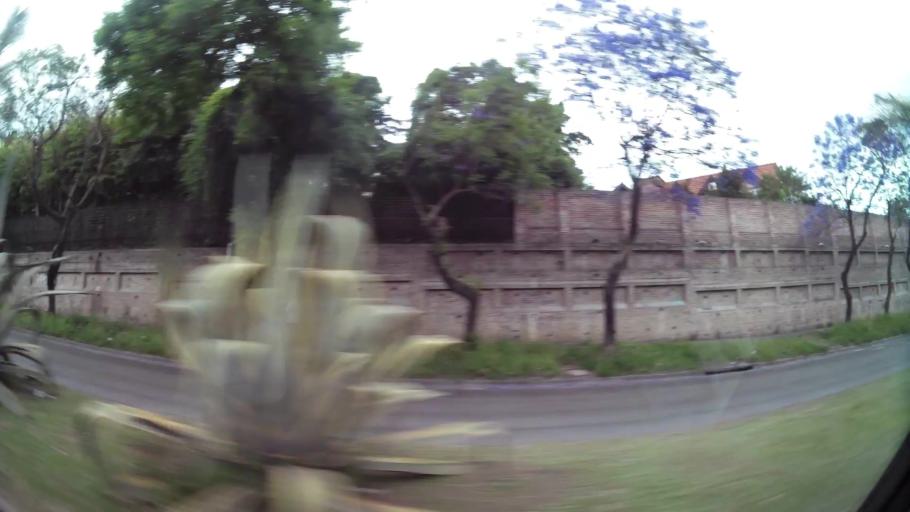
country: AR
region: Buenos Aires
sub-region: Partido de Tigre
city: Tigre
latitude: -34.4758
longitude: -58.5766
